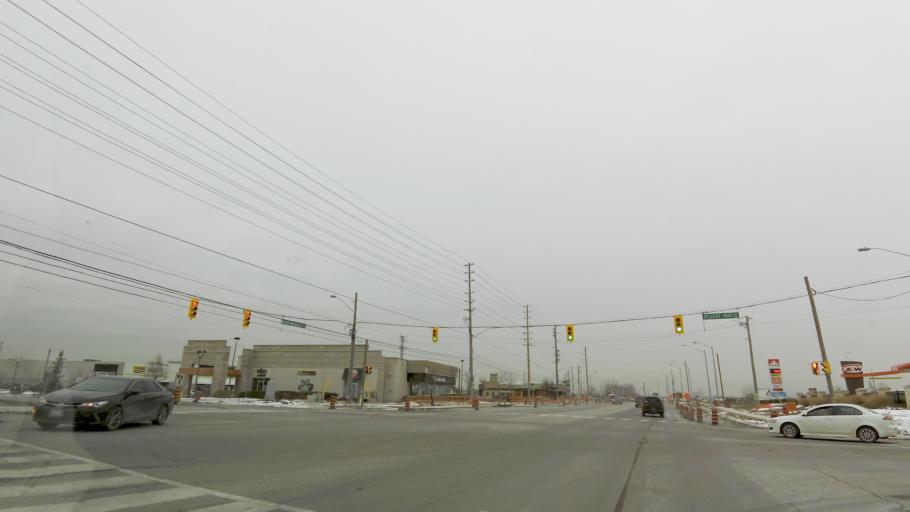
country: CA
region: Ontario
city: Vaughan
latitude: 43.8452
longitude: -79.5562
